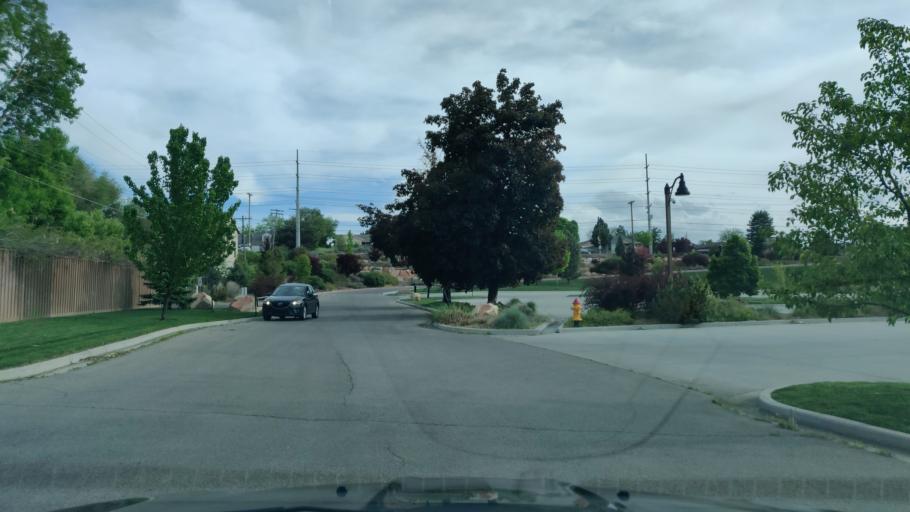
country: US
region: Utah
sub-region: Salt Lake County
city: Little Cottonwood Creek Valley
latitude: 40.6266
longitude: -111.8448
